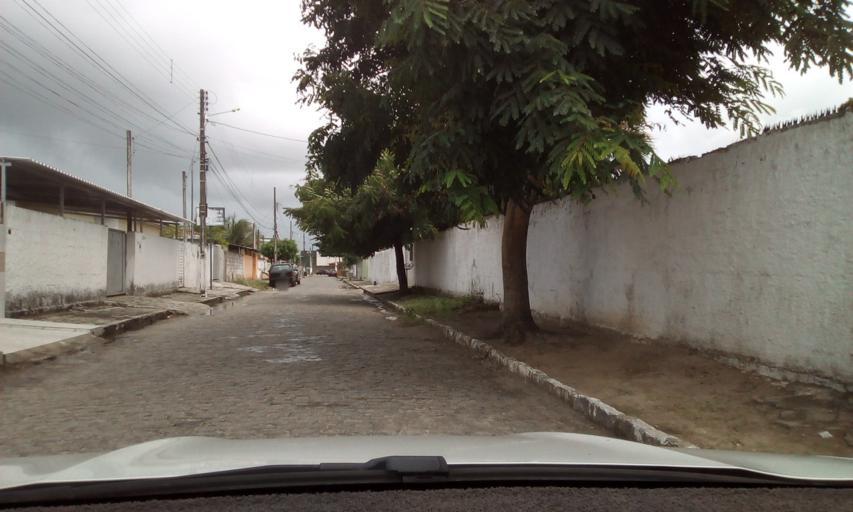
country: BR
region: Paraiba
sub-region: Santa Rita
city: Santa Rita
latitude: -7.1407
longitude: -34.9663
